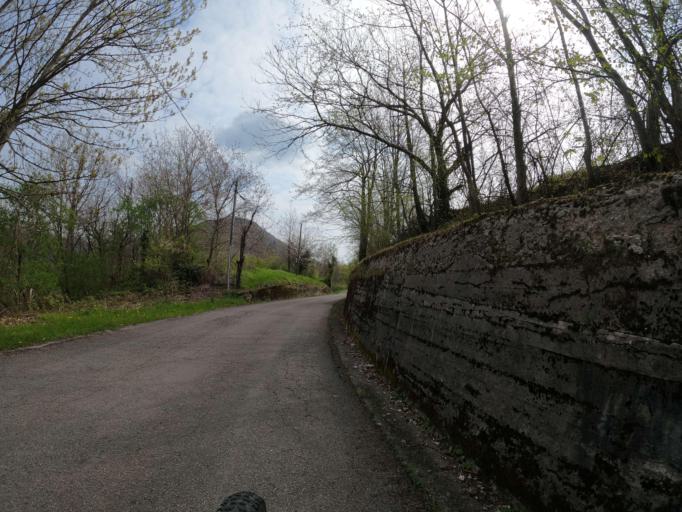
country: IT
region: Friuli Venezia Giulia
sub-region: Provincia di Udine
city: Clodig
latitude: 46.1448
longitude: 13.6095
